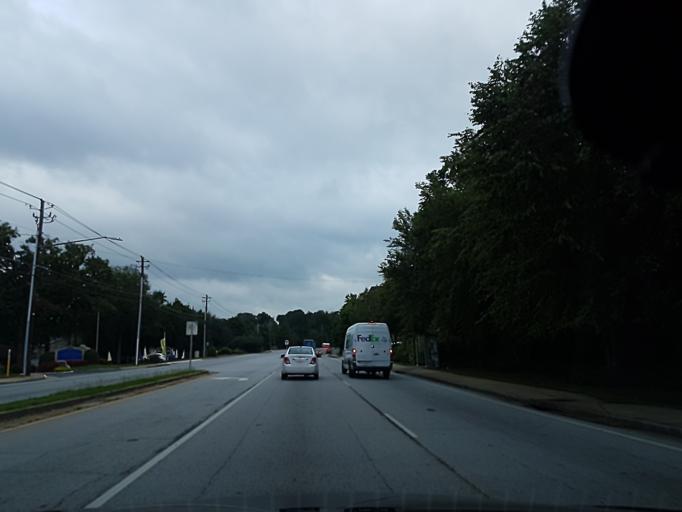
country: US
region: Georgia
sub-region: DeKalb County
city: Stone Mountain
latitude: 33.8216
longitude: -84.1945
